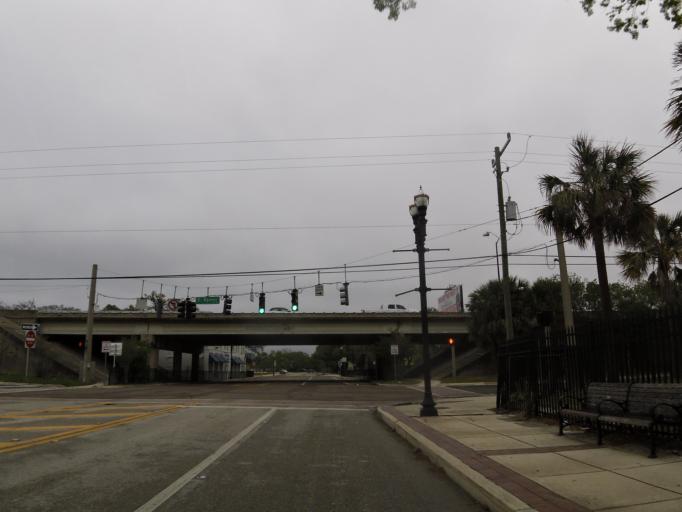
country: US
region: Florida
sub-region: Duval County
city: Jacksonville
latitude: 30.3279
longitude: -81.6430
